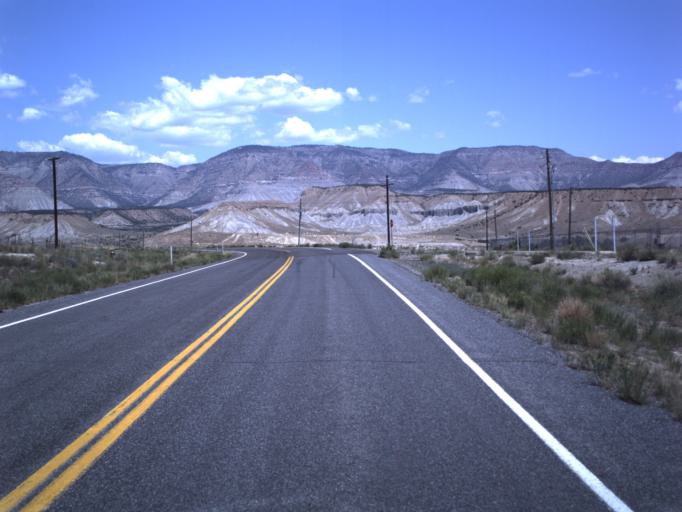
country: US
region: Utah
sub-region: Emery County
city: Orangeville
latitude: 39.2384
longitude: -111.0881
